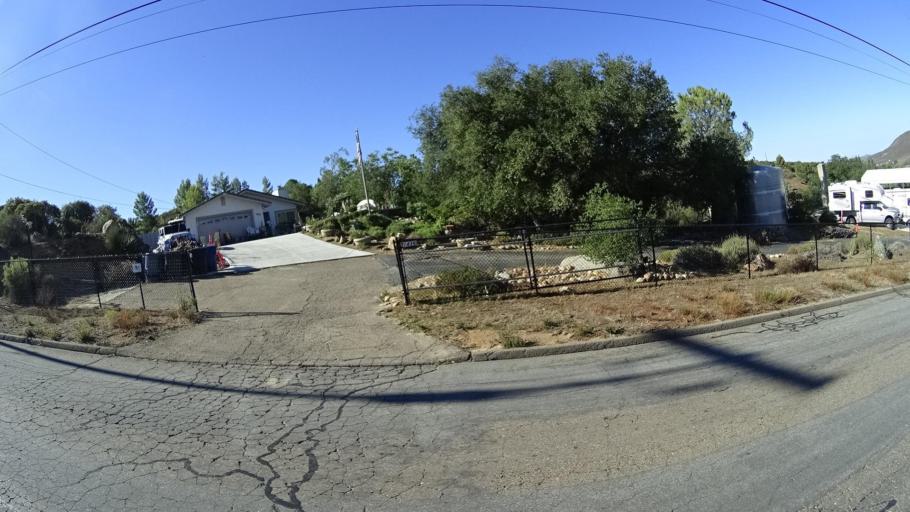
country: US
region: California
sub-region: San Diego County
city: Alpine
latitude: 32.8364
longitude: -116.7013
